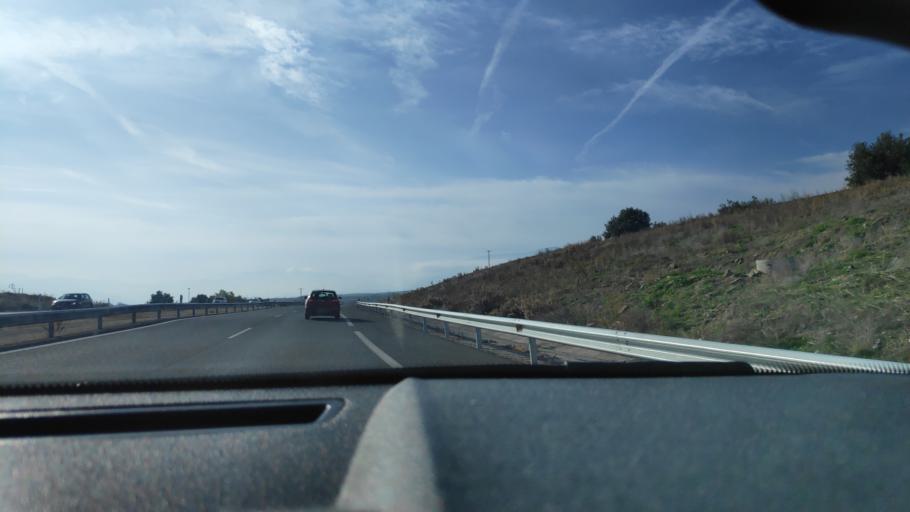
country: ES
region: Andalusia
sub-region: Provincia de Jaen
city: Jaen
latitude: 37.8629
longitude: -3.7641
